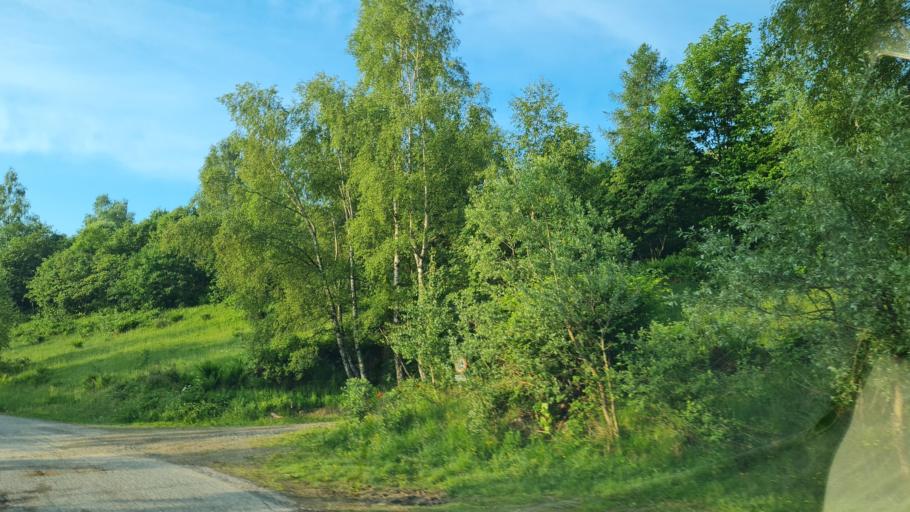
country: IT
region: Piedmont
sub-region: Provincia di Biella
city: Sordevolo
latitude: 45.6064
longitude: 7.9827
